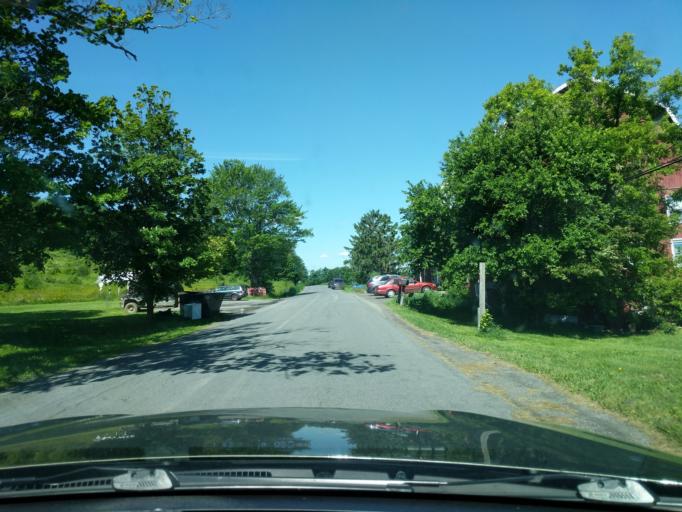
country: US
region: New York
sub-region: Tompkins County
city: East Ithaca
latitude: 42.3804
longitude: -76.3658
